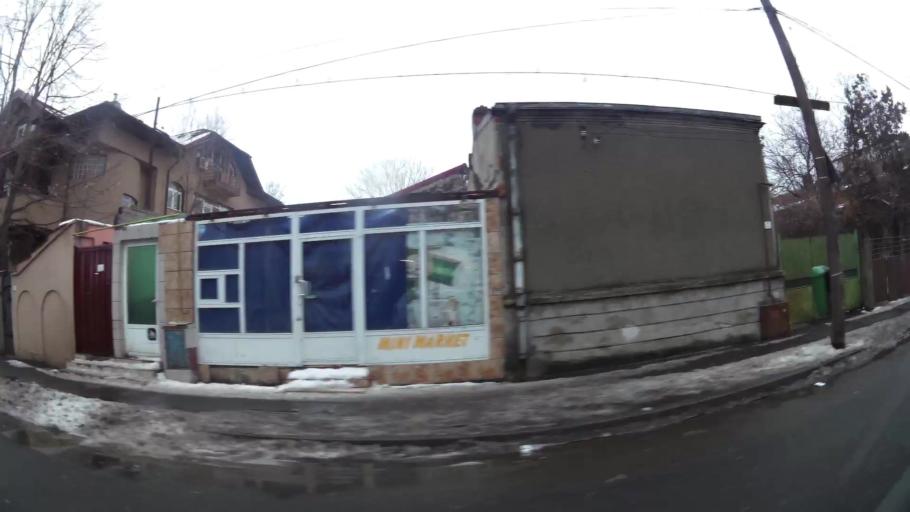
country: RO
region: Ilfov
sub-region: Comuna Chiajna
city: Rosu
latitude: 44.4514
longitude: 26.0539
